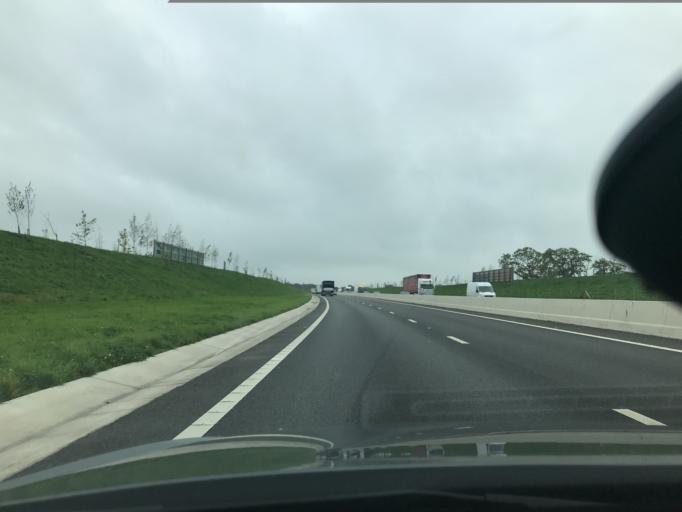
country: GB
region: England
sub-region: Cheshire East
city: Mere
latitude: 53.3449
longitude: -2.4139
